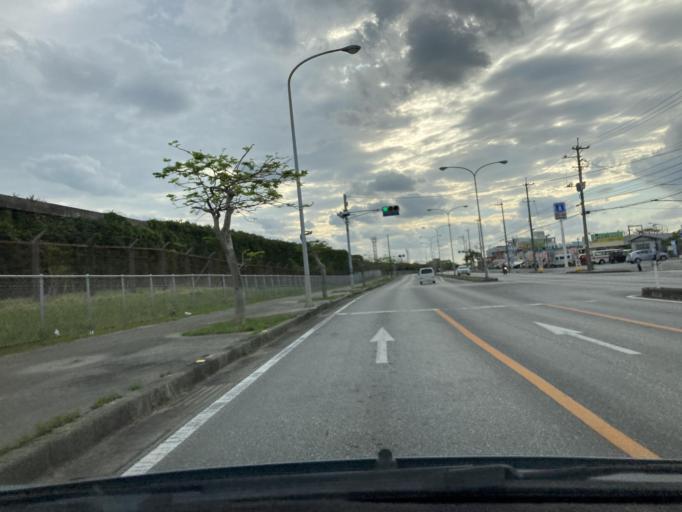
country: JP
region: Okinawa
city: Okinawa
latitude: 26.3666
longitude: 127.7730
